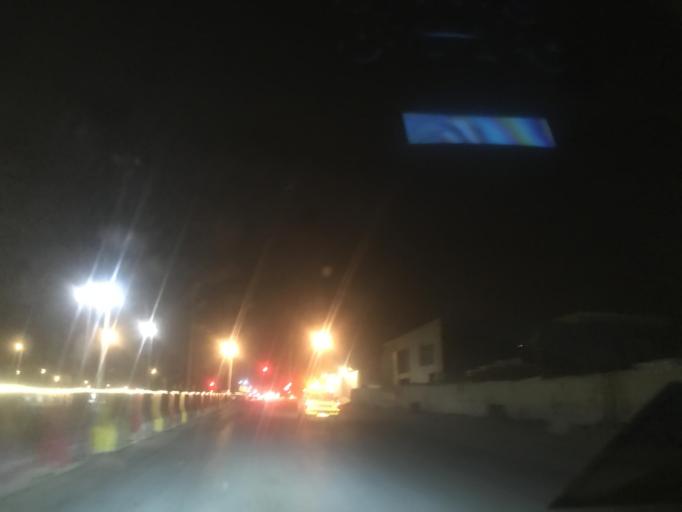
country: SA
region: Ar Riyad
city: Riyadh
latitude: 24.7957
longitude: 46.5881
